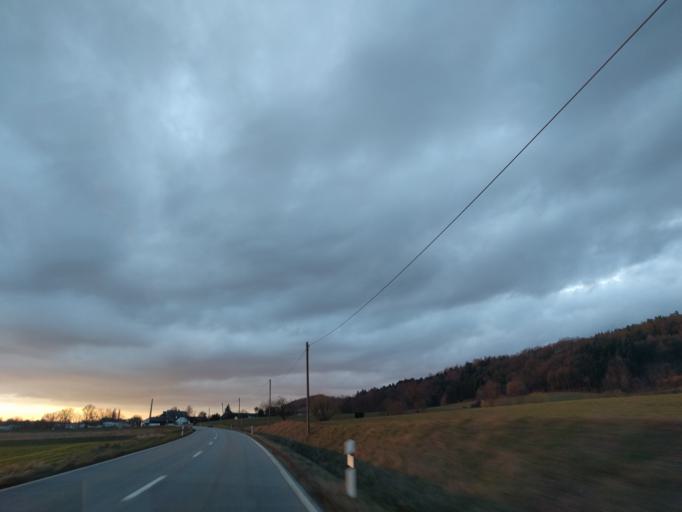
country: DE
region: Bavaria
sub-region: Lower Bavaria
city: Winzer
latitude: 48.7149
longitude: 13.0998
